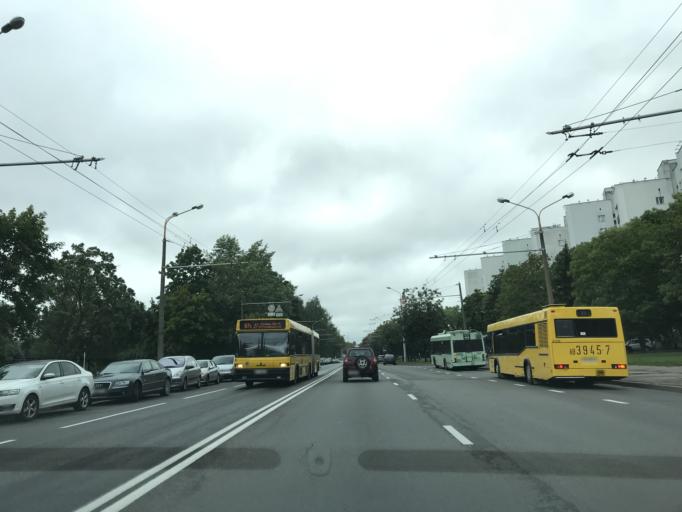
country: BY
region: Minsk
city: Borovlyany
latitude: 53.9372
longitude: 27.6414
